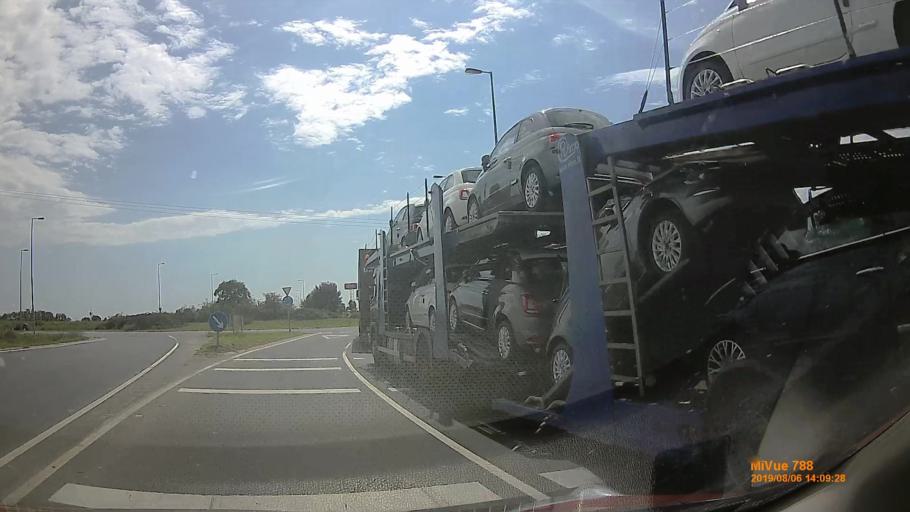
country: HU
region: Vas
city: Szombathely
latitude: 47.2320
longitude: 16.6570
